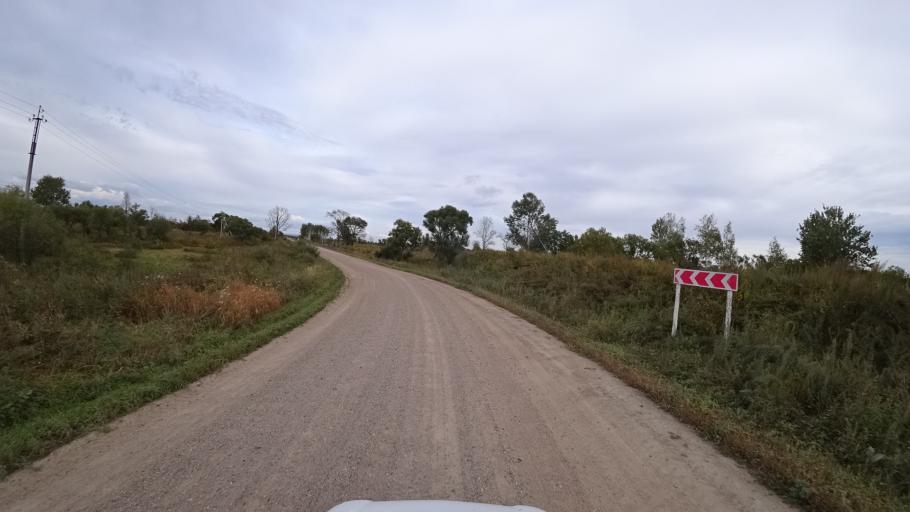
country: RU
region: Amur
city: Arkhara
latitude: 49.3761
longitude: 130.1700
